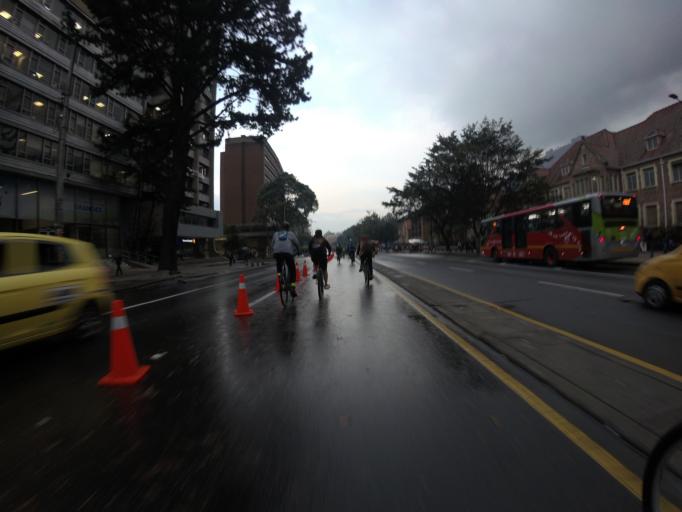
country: CO
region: Bogota D.C.
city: Bogota
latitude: 4.6220
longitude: -74.0669
